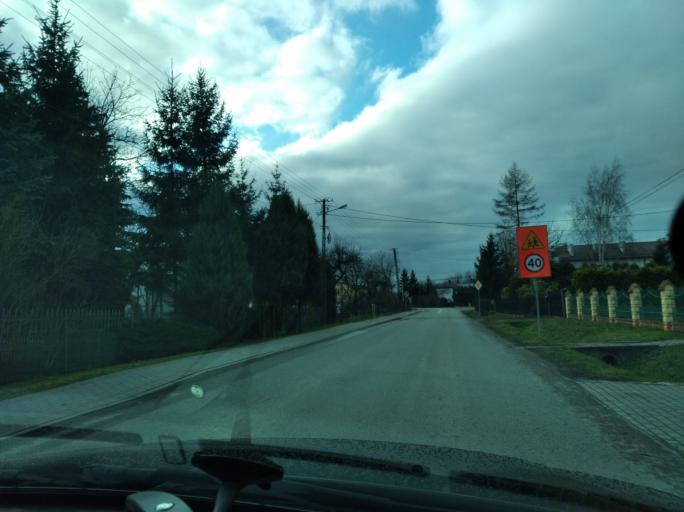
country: PL
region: Subcarpathian Voivodeship
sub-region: Powiat lancucki
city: Gluchow
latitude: 50.1074
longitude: 22.2613
